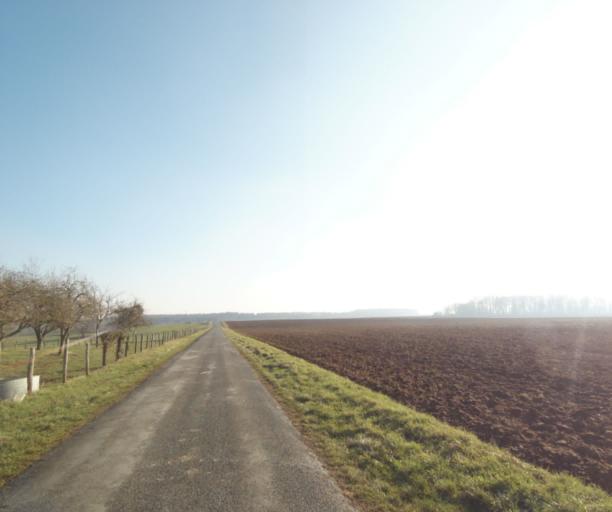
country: FR
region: Champagne-Ardenne
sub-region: Departement de la Haute-Marne
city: Bienville
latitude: 48.5040
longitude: 5.0386
